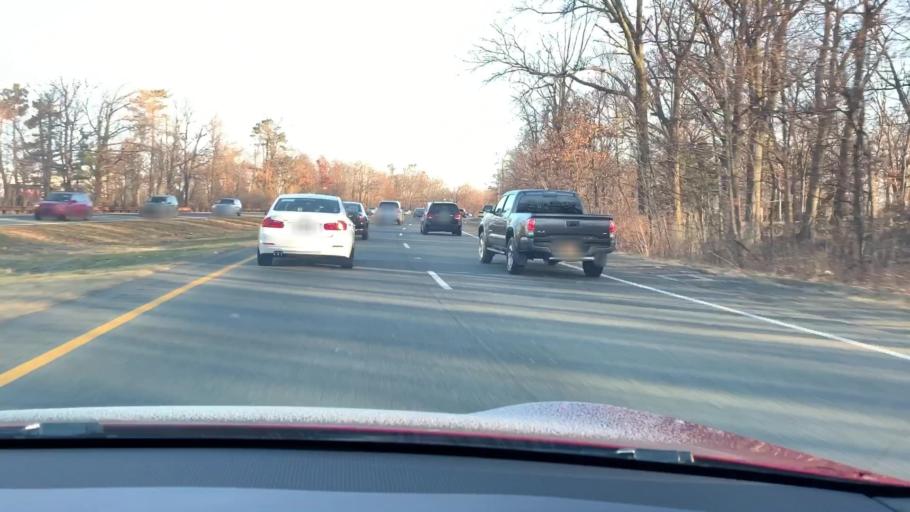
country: US
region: New Jersey
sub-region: Bergen County
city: Englewood Cliffs
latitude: 40.8691
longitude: -73.9539
